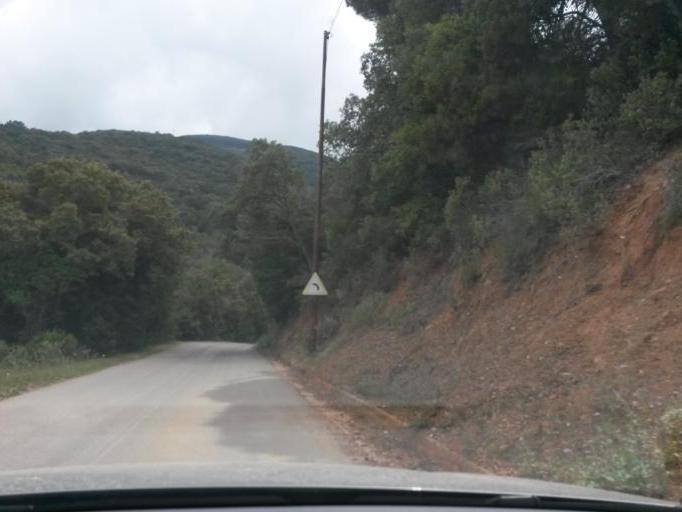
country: IT
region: Tuscany
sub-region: Provincia di Livorno
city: Porto Azzurro
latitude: 42.7456
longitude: 10.3997
